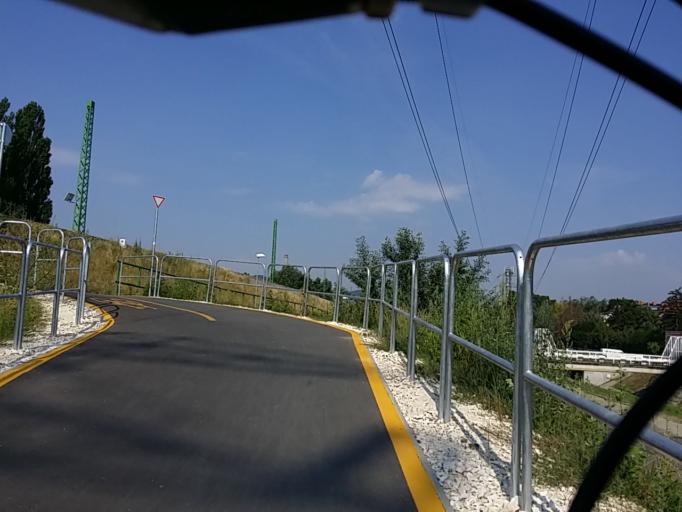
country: HU
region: Budapest
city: Budapest IV. keruelet
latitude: 47.5646
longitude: 19.0626
